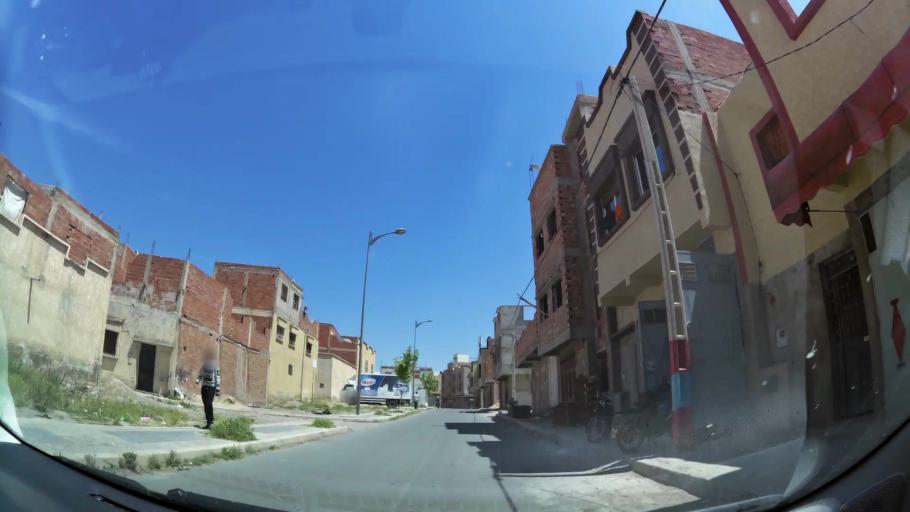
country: MA
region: Oriental
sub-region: Oujda-Angad
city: Oujda
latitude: 34.6891
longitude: -1.9536
